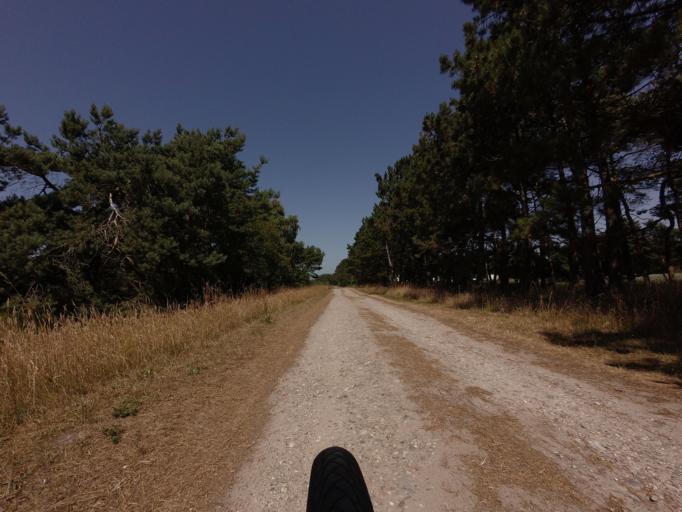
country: DK
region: North Denmark
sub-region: Laeso Kommune
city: Byrum
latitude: 57.2545
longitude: 10.9167
